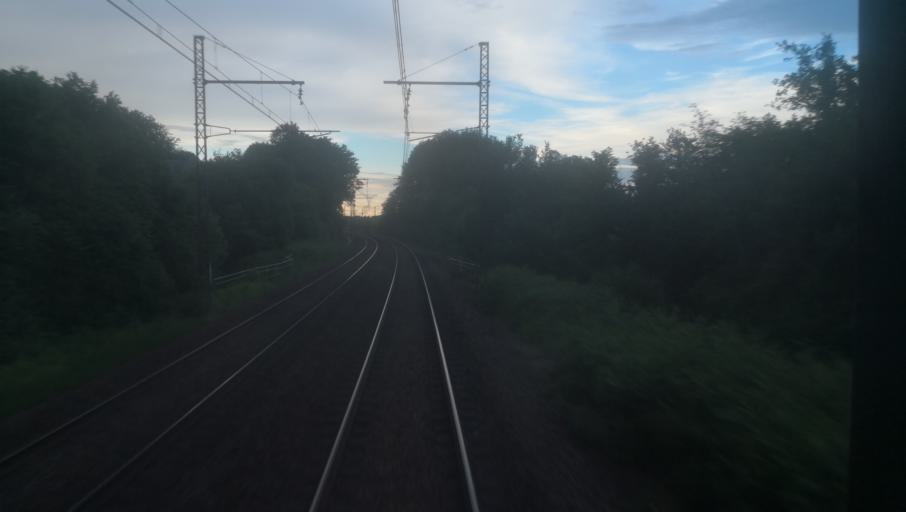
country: FR
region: Limousin
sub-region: Departement de la Haute-Vienne
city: Bessines-sur-Gartempe
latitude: 46.0796
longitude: 1.4315
